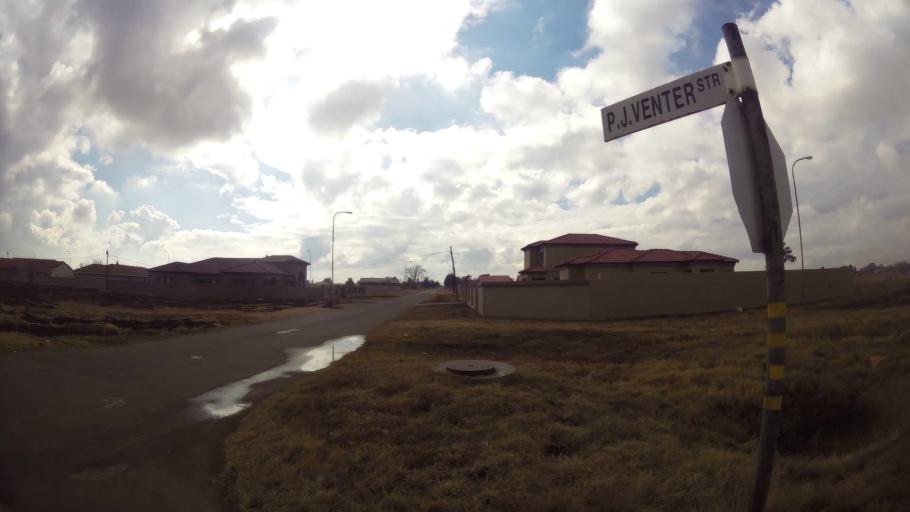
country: ZA
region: Gauteng
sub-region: Sedibeng District Municipality
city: Meyerton
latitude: -26.6120
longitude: 28.0492
